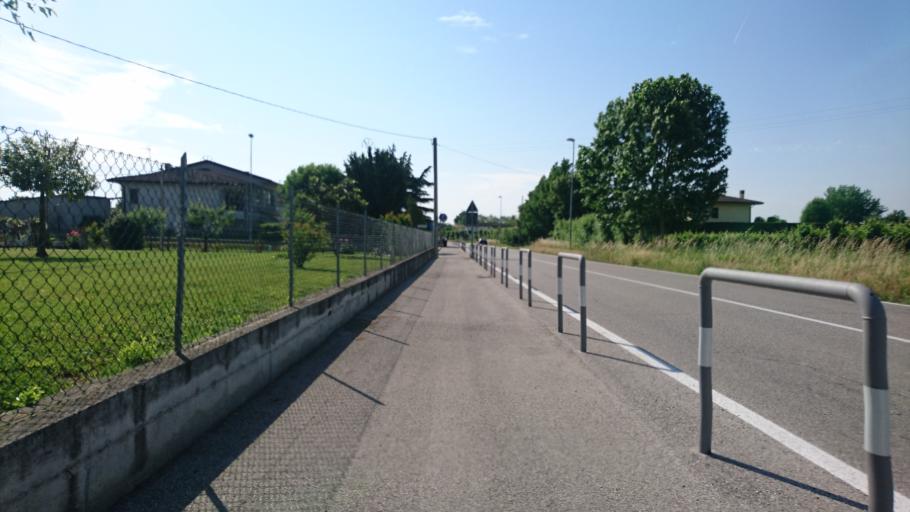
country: IT
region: Veneto
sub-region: Provincia di Padova
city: Merlara
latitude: 45.1732
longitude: 11.4295
